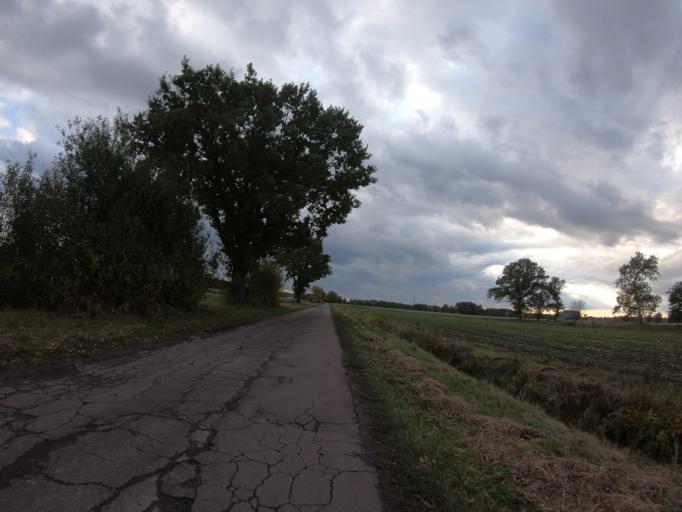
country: DE
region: Lower Saxony
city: Wagenhoff
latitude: 52.5380
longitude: 10.5445
